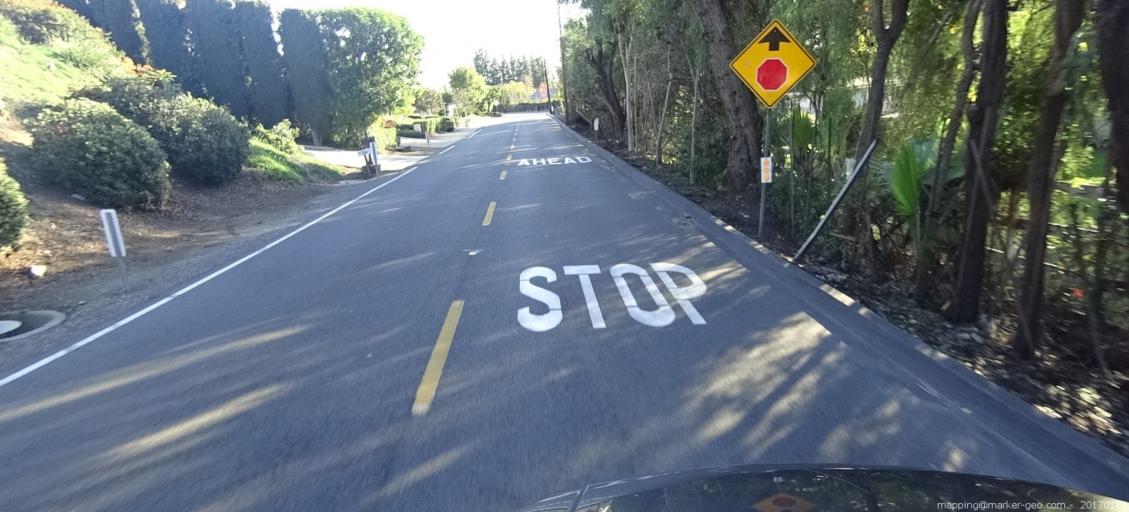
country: US
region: California
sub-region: Orange County
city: North Tustin
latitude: 33.7748
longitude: -117.8012
